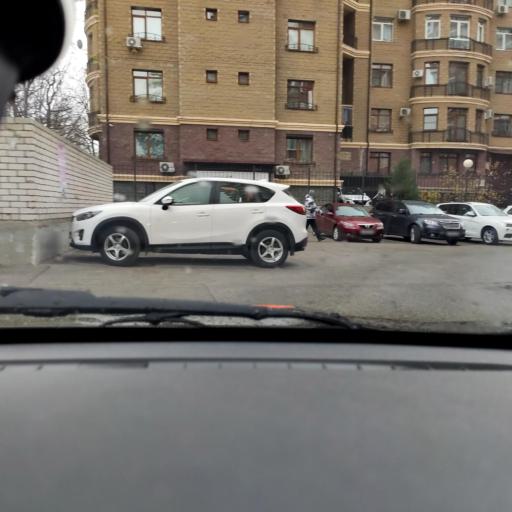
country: RU
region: Samara
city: Tol'yatti
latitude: 53.5365
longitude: 49.3623
